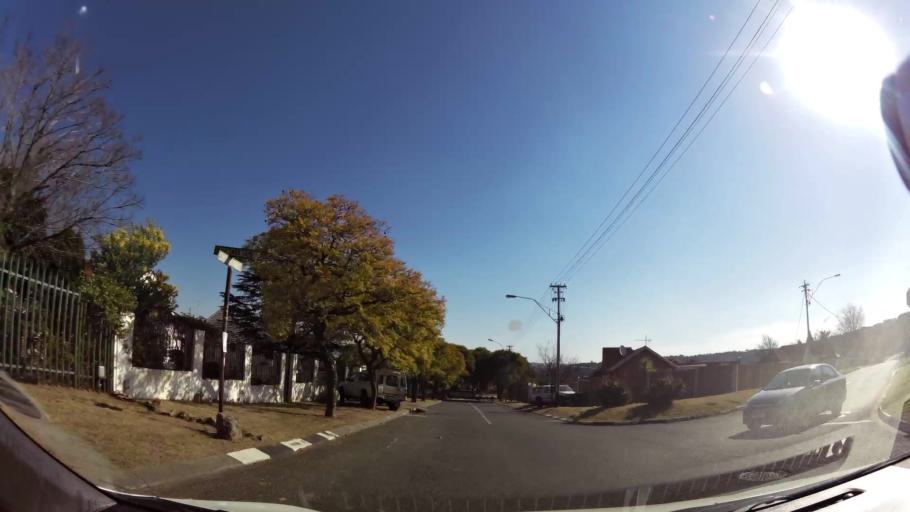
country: ZA
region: Gauteng
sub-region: City of Johannesburg Metropolitan Municipality
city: Johannesburg
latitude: -26.2725
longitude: 28.0157
